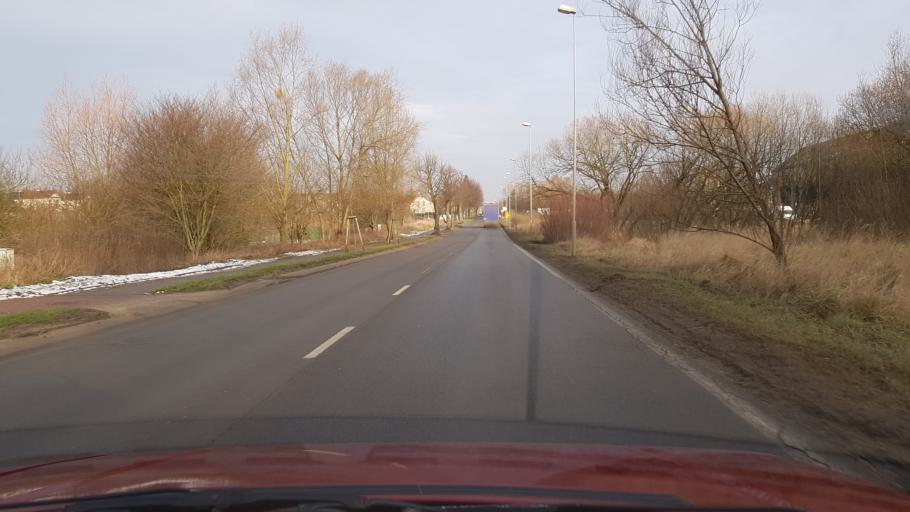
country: PL
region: West Pomeranian Voivodeship
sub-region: Powiat policki
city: Police
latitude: 53.4890
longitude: 14.5851
